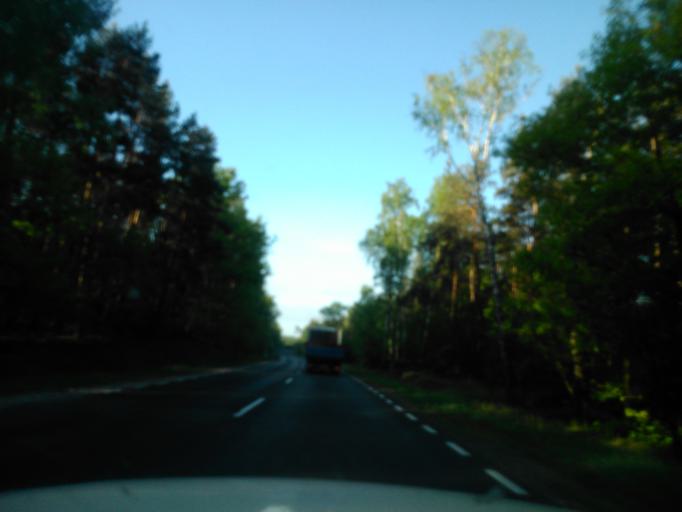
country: PL
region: Masovian Voivodeship
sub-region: Powiat sochaczewski
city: Mlodzieszyn
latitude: 52.3186
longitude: 20.2072
